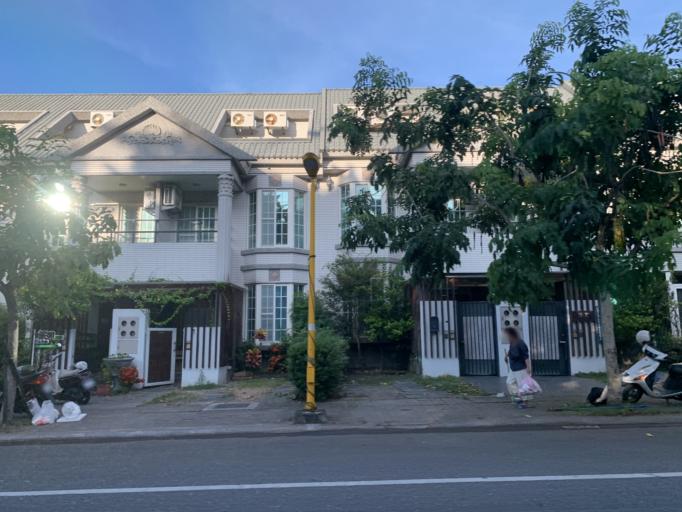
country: TW
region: Taiwan
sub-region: Hualien
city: Hualian
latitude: 23.9992
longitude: 121.6295
